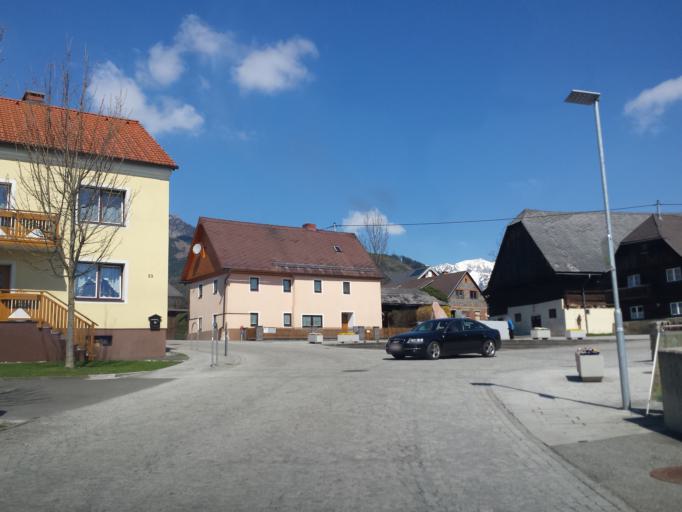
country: AT
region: Styria
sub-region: Politischer Bezirk Leoben
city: Trofaiach
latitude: 47.4184
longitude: 14.9594
